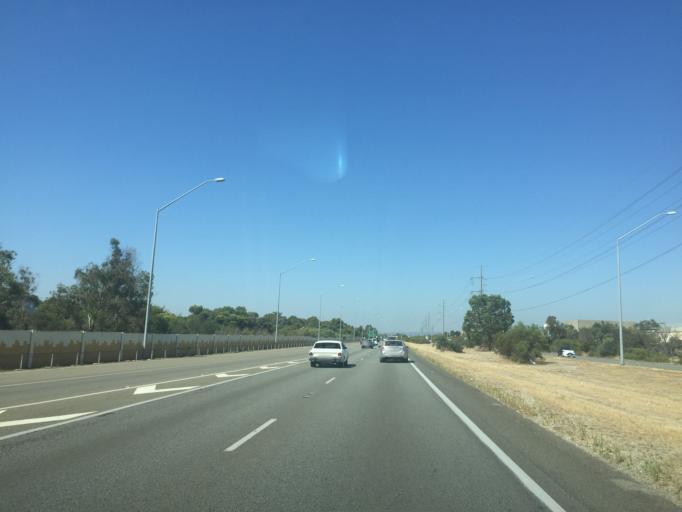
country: AU
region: Western Australia
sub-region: Canning
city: Willetton
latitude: -32.0655
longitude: 115.8941
